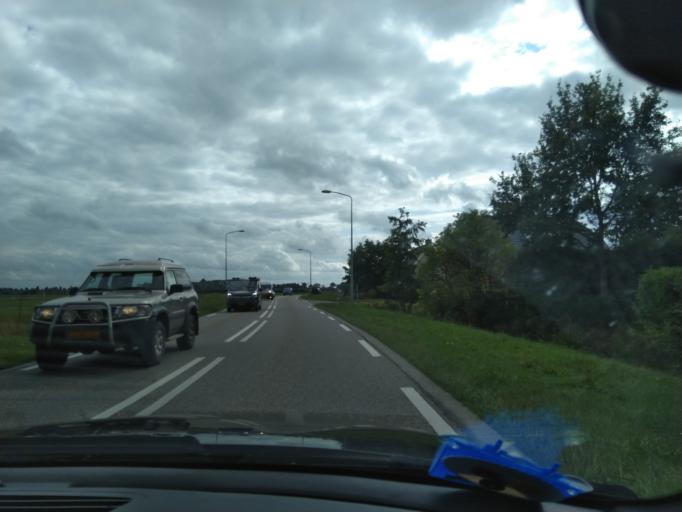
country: NL
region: Groningen
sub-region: Gemeente Zuidhorn
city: Grijpskerk
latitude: 53.2615
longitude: 6.3162
